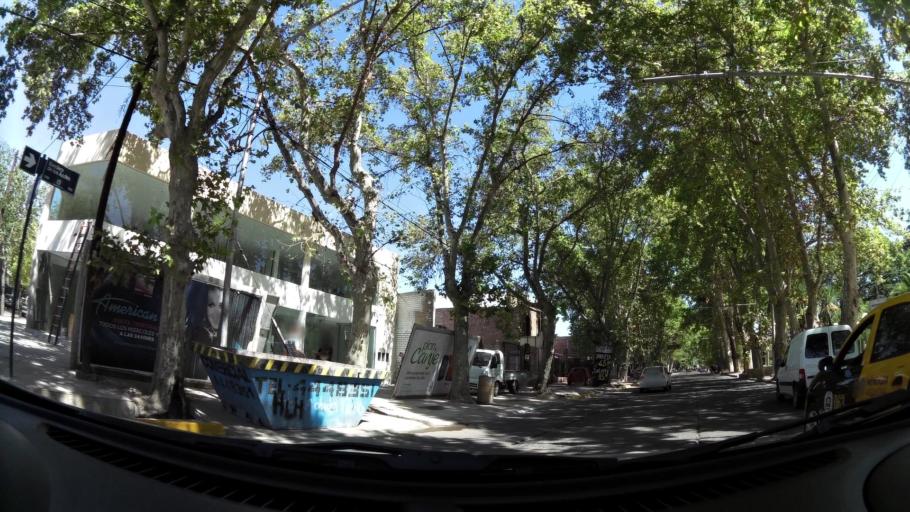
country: AR
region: Mendoza
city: Mendoza
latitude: -32.8942
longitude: -68.8240
